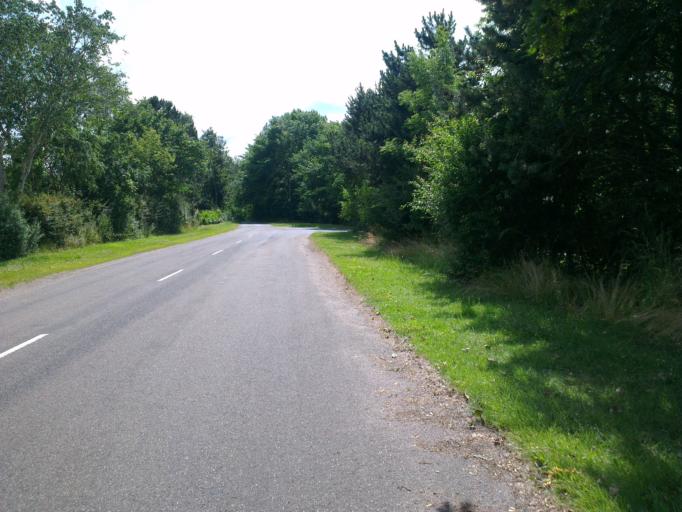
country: DK
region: Zealand
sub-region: Lejre Kommune
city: Ejby
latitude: 55.7397
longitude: 11.8632
